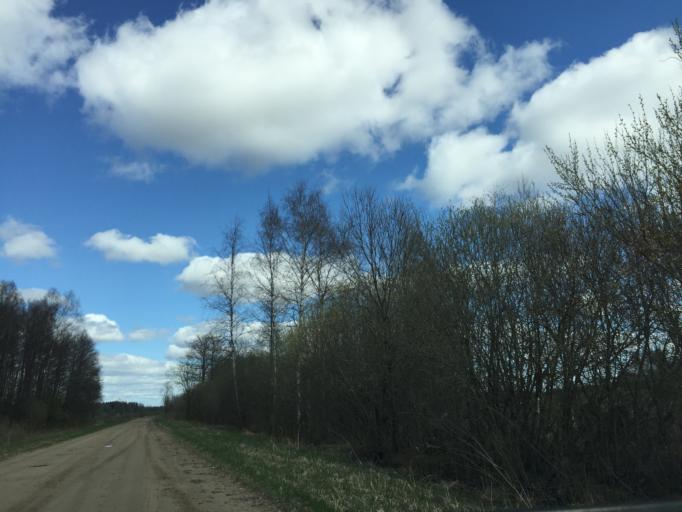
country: LV
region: Vilanu
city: Vilani
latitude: 56.6783
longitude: 27.0957
